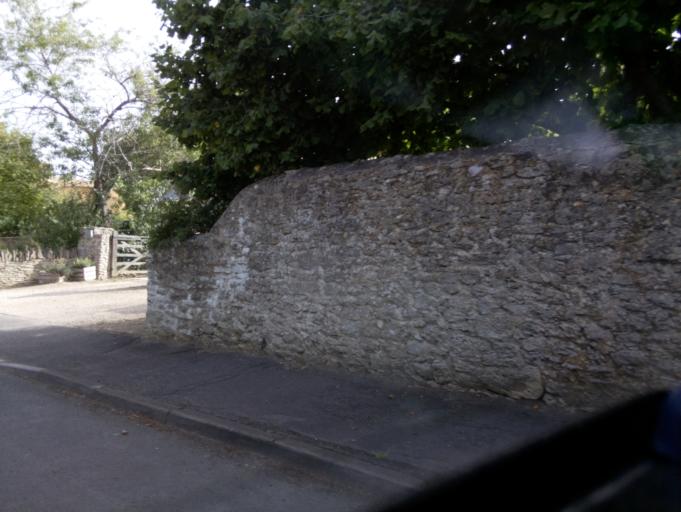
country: GB
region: England
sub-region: Borough of Swindon
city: Hannington
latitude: 51.6138
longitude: -1.7475
